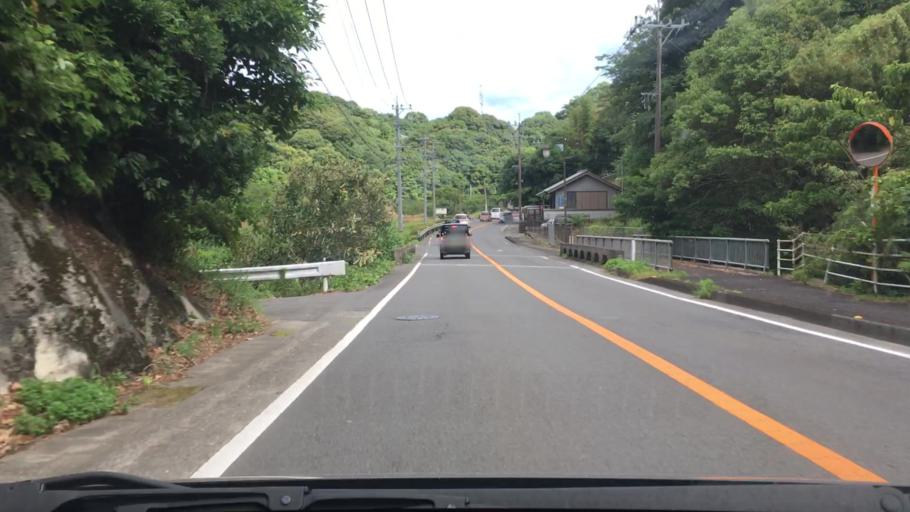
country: JP
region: Nagasaki
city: Togitsu
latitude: 32.9563
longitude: 129.7838
